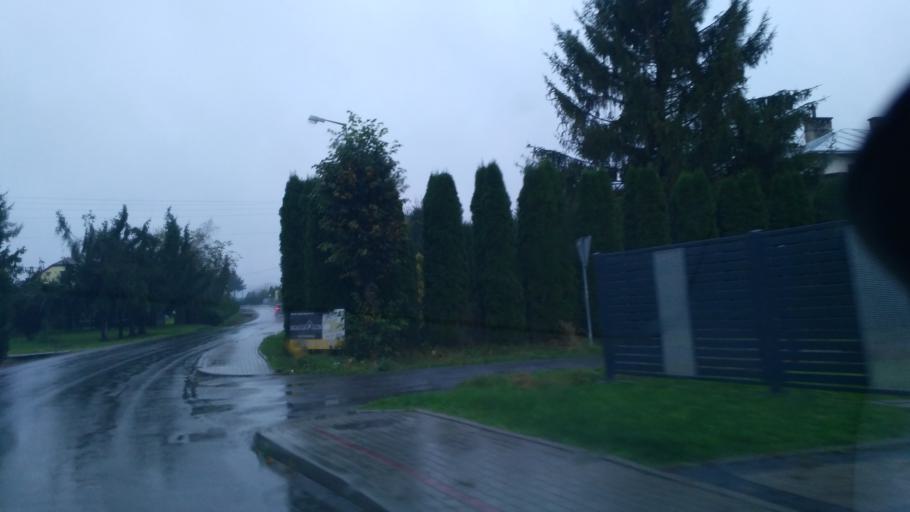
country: PL
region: Subcarpathian Voivodeship
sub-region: Powiat krosnienski
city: Korczyna
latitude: 49.7025
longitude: 21.8125
